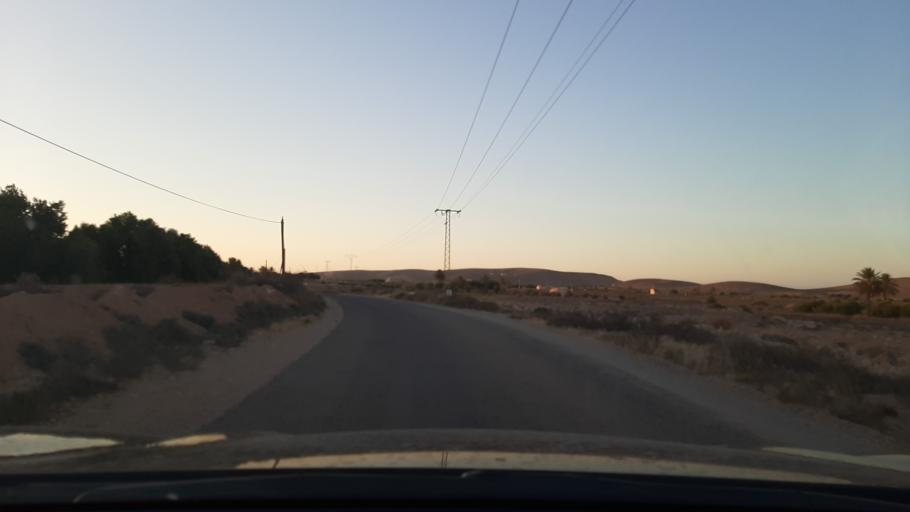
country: TN
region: Qabis
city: Matmata
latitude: 33.5558
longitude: 10.1854
